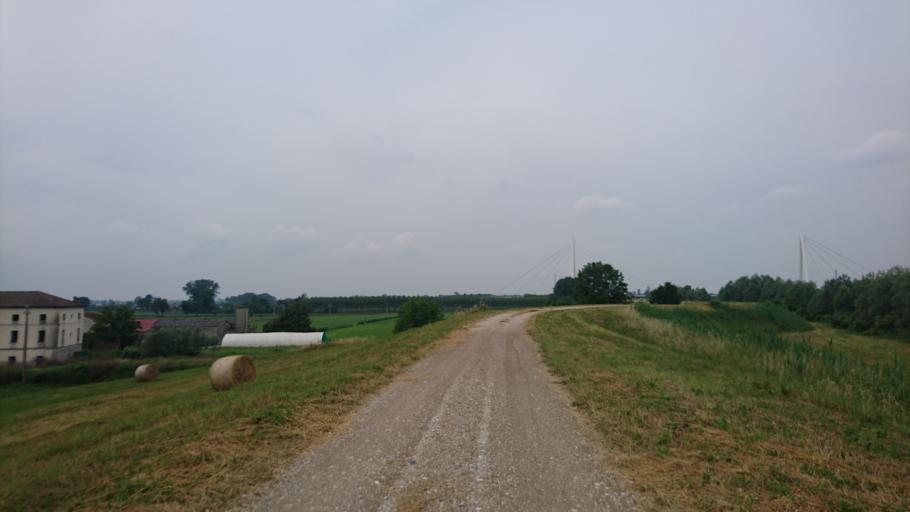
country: IT
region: Veneto
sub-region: Provincia di Padova
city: Piacenza d'Adige
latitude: 45.1195
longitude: 11.5409
